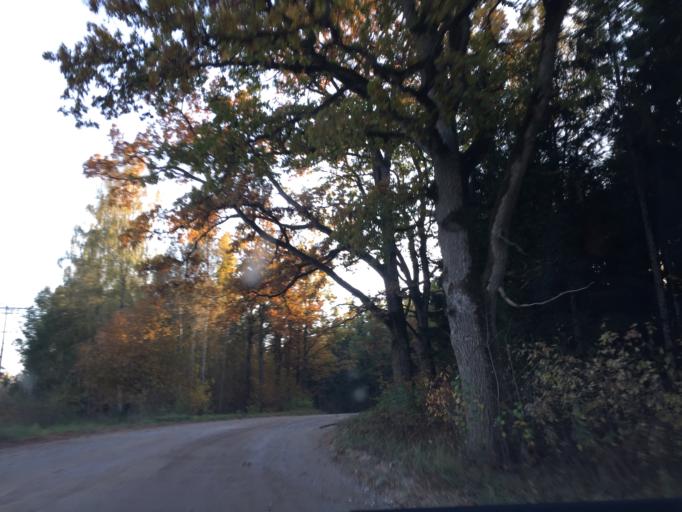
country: LV
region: Vainode
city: Vainode
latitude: 56.6040
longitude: 21.8252
